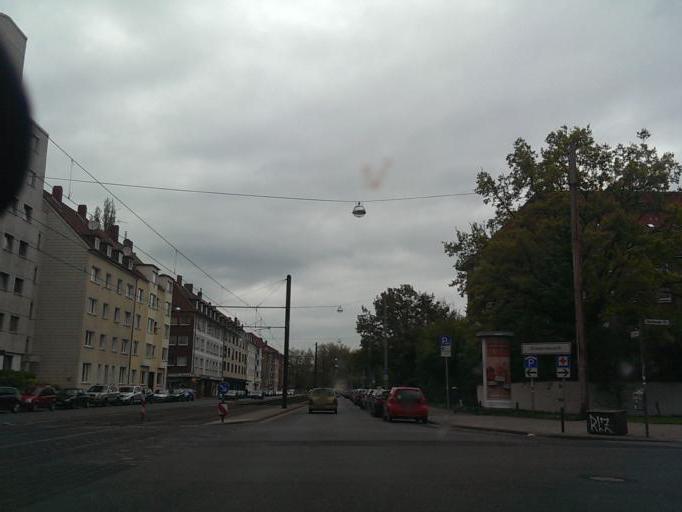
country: DE
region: Lower Saxony
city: Hannover
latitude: 52.3697
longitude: 9.7232
